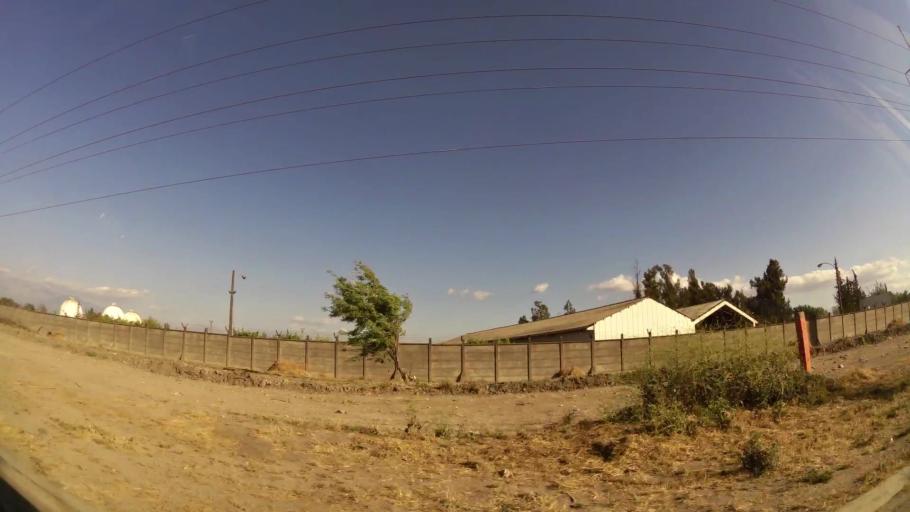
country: CL
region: Santiago Metropolitan
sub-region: Provincia de Maipo
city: San Bernardo
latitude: -33.5389
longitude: -70.7629
